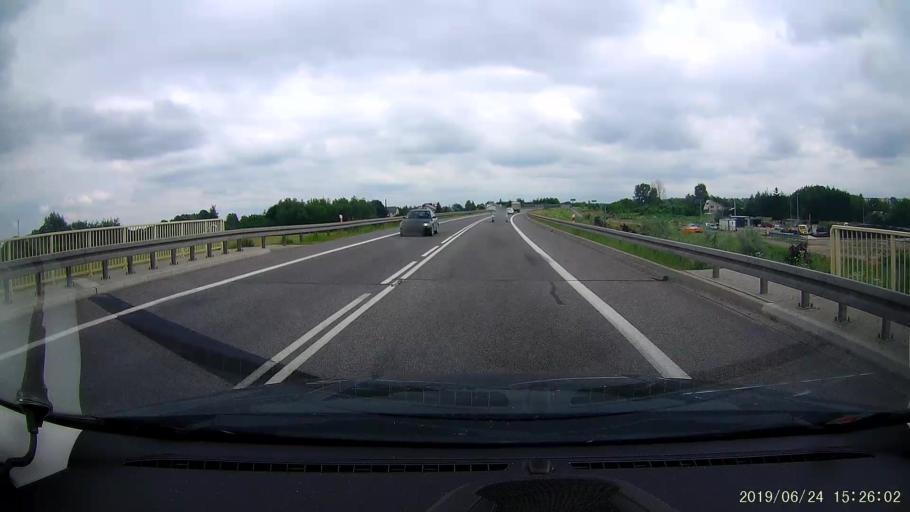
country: PL
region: Subcarpathian Voivodeship
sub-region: Powiat jaroslawski
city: Jaroslaw
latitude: 50.0282
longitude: 22.6897
